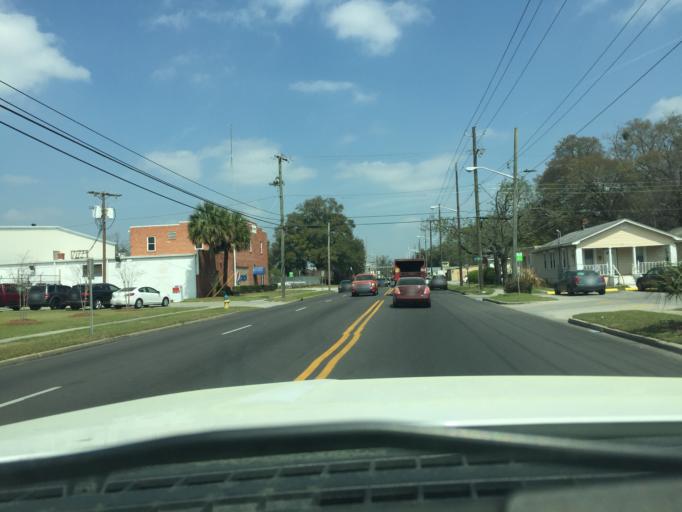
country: US
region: Georgia
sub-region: Chatham County
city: Savannah
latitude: 32.0425
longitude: -81.1103
